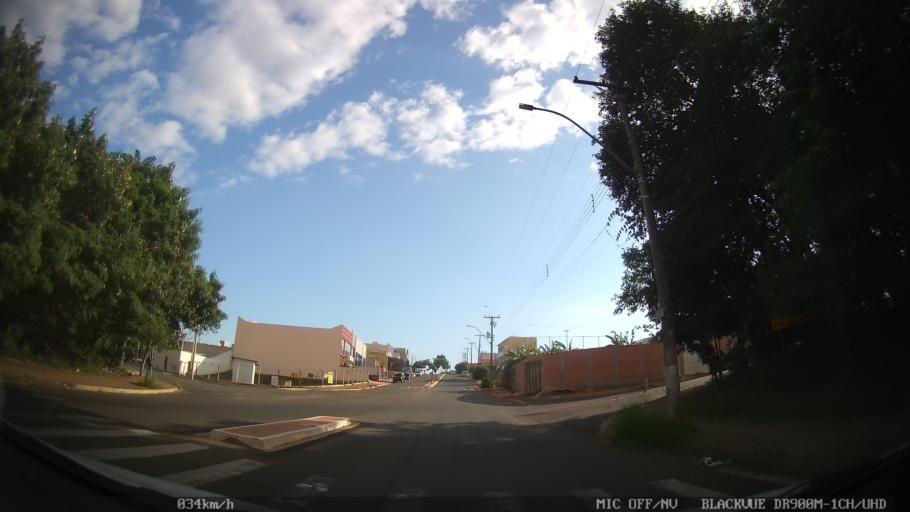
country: BR
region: Sao Paulo
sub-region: Americana
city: Americana
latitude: -22.7286
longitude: -47.3669
